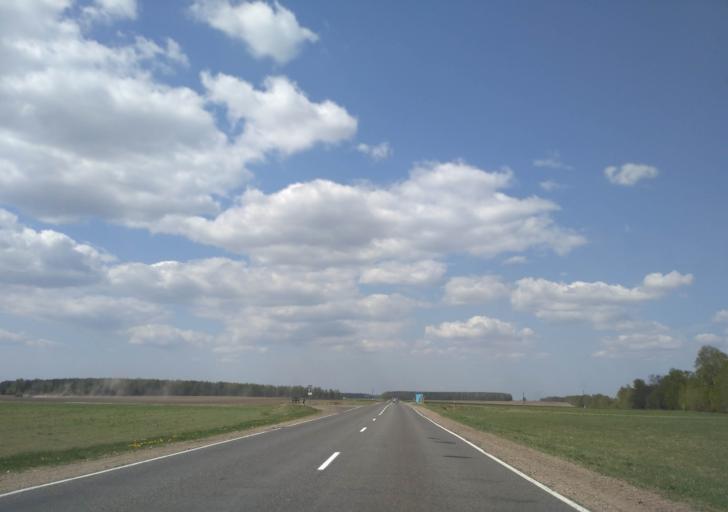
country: BY
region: Minsk
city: Vilyeyka
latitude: 54.5125
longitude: 27.0486
